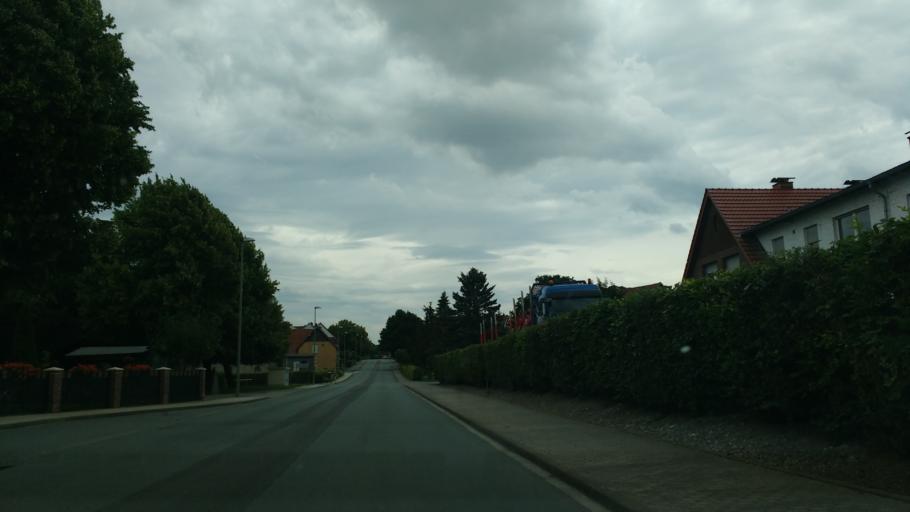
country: DE
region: North Rhine-Westphalia
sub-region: Regierungsbezirk Detmold
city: Wunnenberg
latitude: 51.5731
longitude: 8.7258
